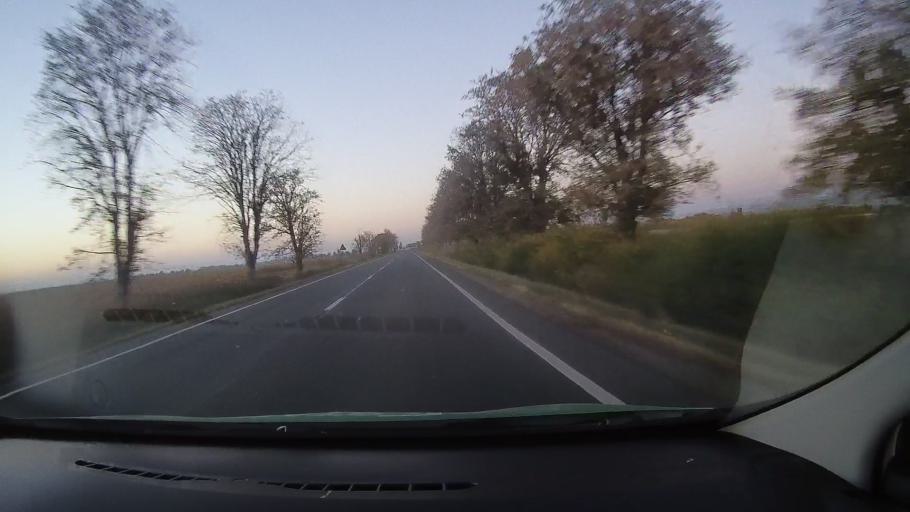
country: RO
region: Bihor
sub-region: Comuna Tarcea
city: Tarcea
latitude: 47.4766
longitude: 22.1638
